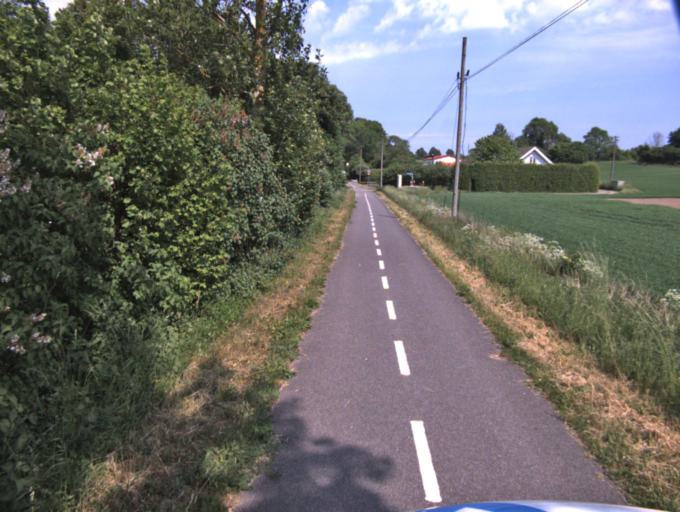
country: SE
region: Skane
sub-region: Kristianstads Kommun
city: Fjalkinge
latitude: 56.0809
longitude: 14.2225
